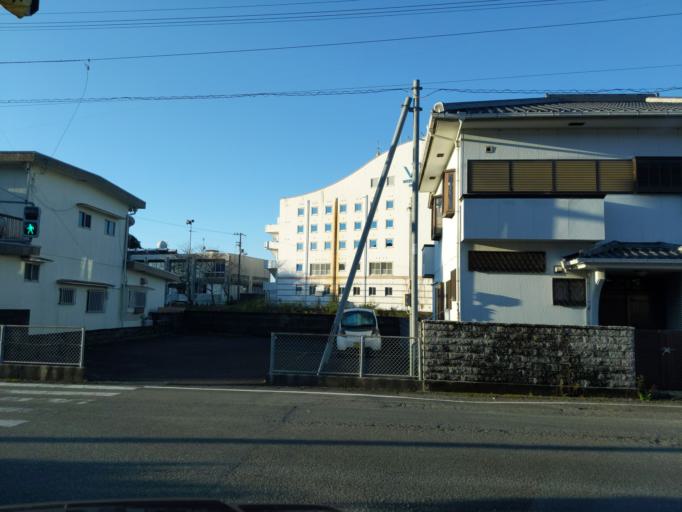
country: JP
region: Kochi
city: Muroto-misakicho
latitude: 33.5443
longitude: 134.2964
